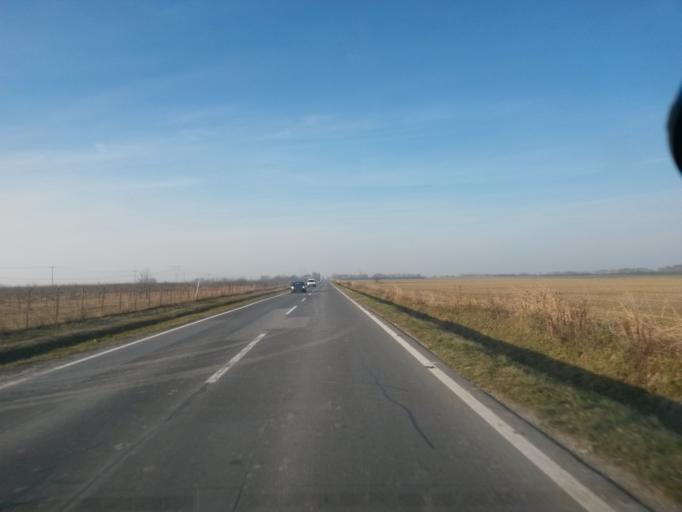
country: HR
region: Osjecko-Baranjska
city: Laslovo
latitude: 45.4263
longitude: 18.6818
